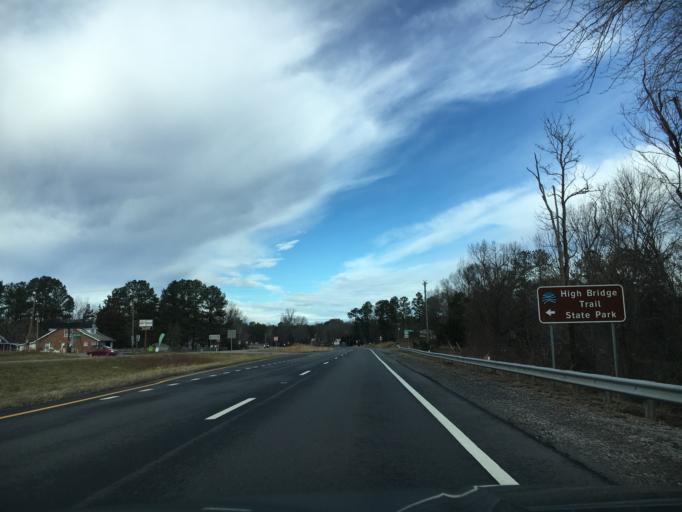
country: US
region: Virginia
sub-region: Nottoway County
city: Crewe
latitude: 37.2338
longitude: -78.2418
